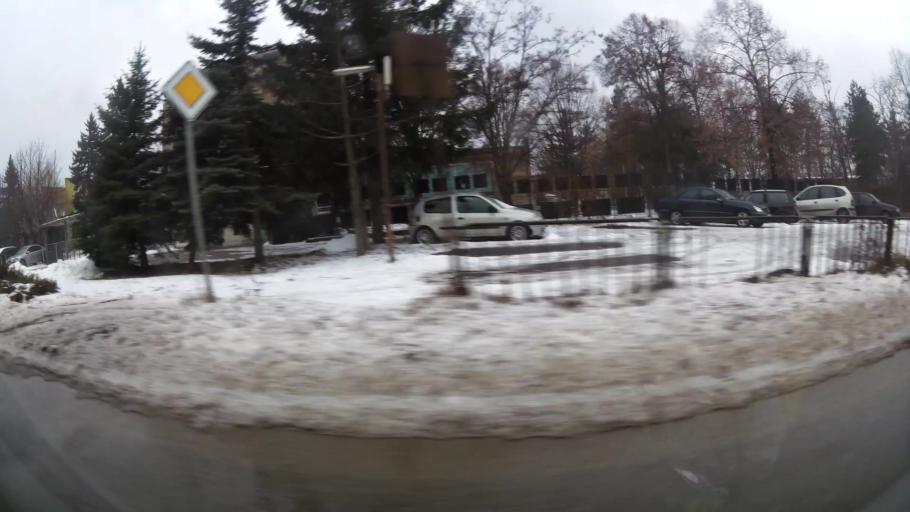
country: BG
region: Sofiya
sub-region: Obshtina Bozhurishte
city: Bozhurishte
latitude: 42.6951
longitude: 23.2480
